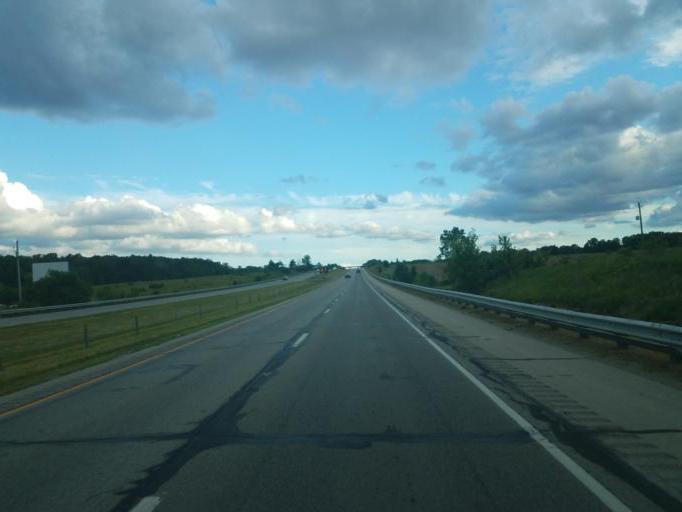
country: US
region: Indiana
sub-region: DeKalb County
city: Garrett
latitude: 41.2882
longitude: -85.0868
